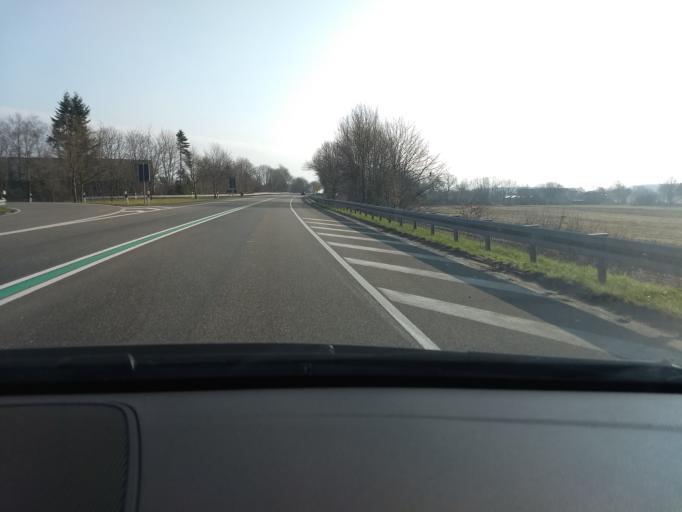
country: DE
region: North Rhine-Westphalia
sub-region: Regierungsbezirk Munster
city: Borken
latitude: 51.8373
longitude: 6.8771
